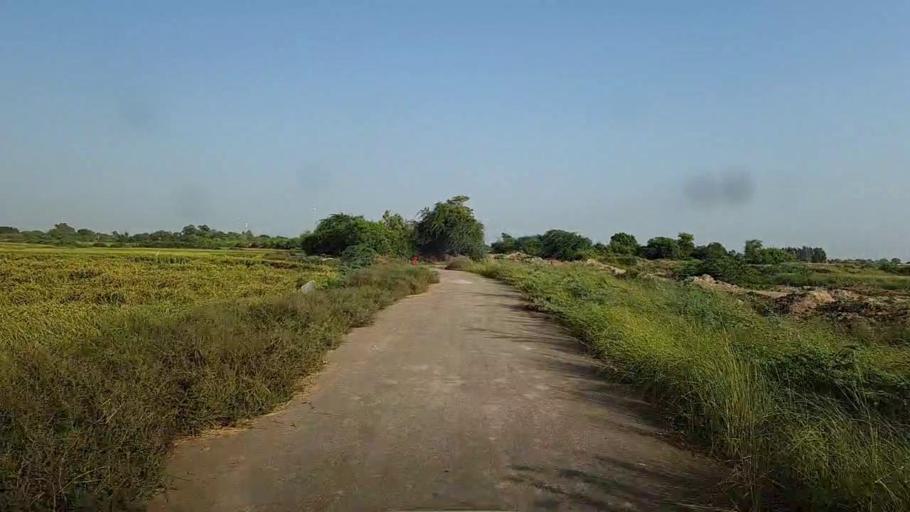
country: PK
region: Sindh
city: Bulri
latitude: 24.7568
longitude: 68.4063
